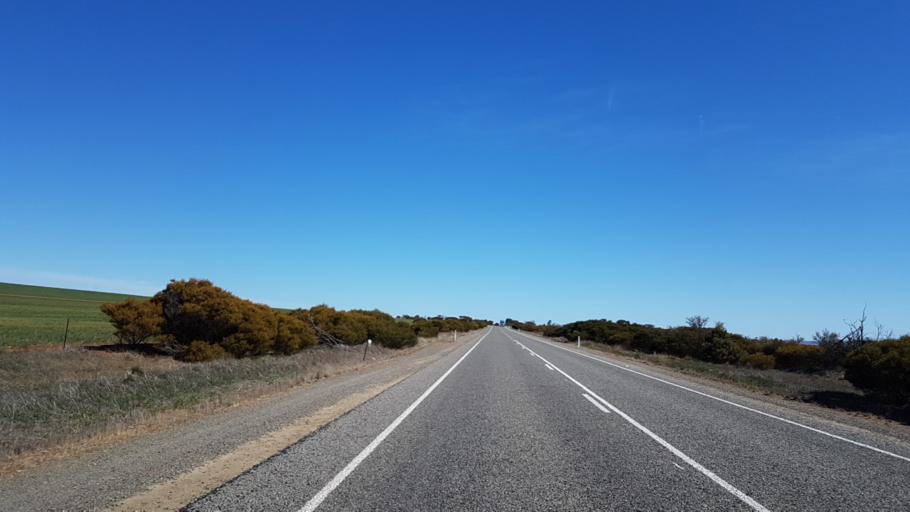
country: AU
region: South Australia
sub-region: Peterborough
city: Peterborough
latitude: -33.2352
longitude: 138.8779
